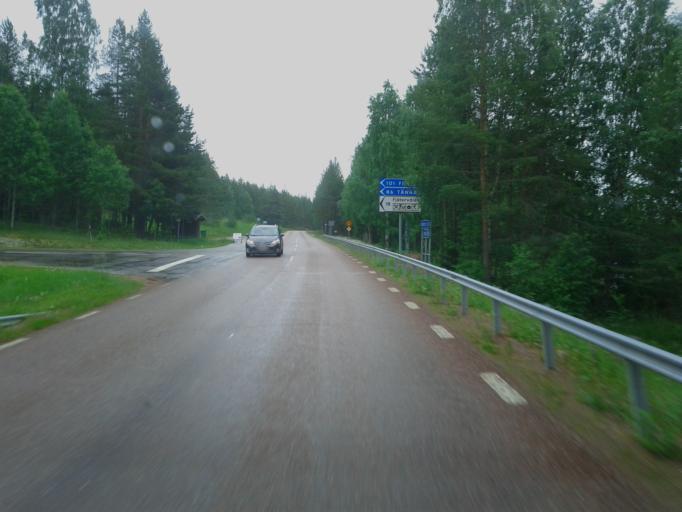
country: NO
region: Hedmark
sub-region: Trysil
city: Innbygda
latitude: 61.7959
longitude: 12.9199
